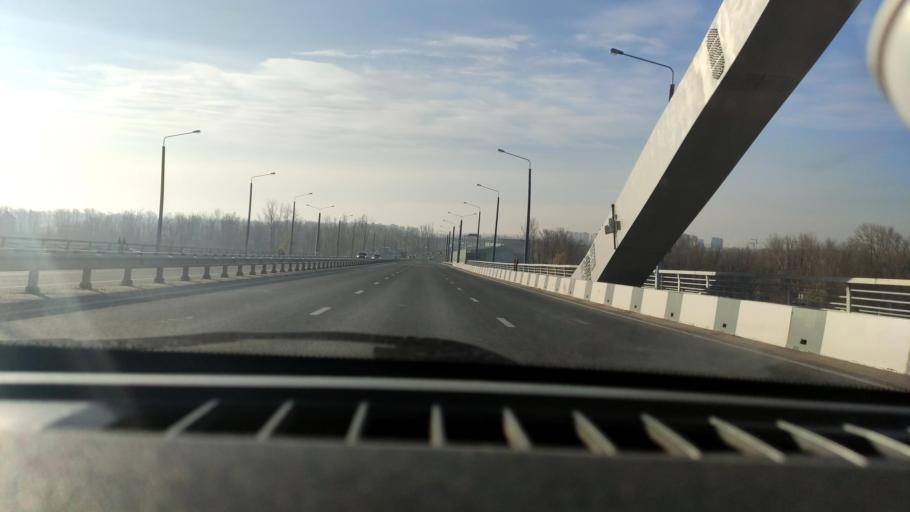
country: RU
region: Samara
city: Rozhdestveno
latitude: 53.1737
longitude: 50.0861
